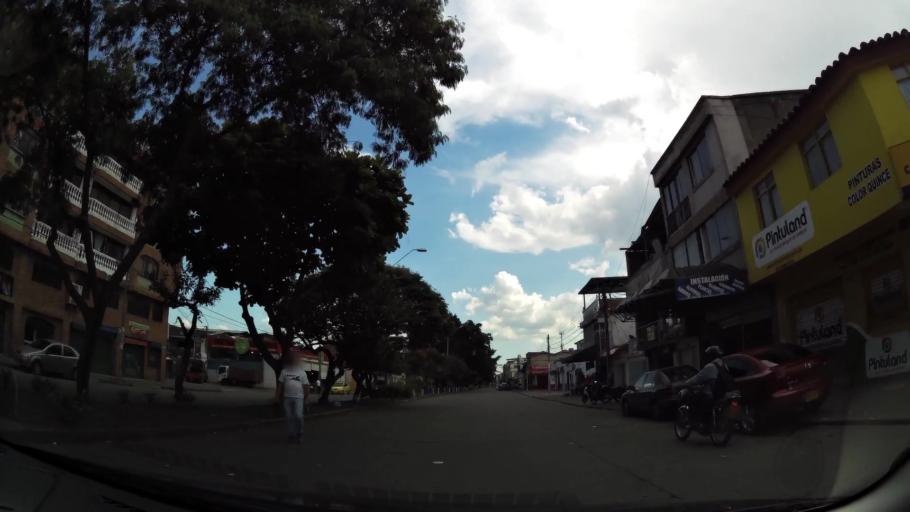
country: CO
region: Valle del Cauca
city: Cali
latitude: 3.4392
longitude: -76.5261
